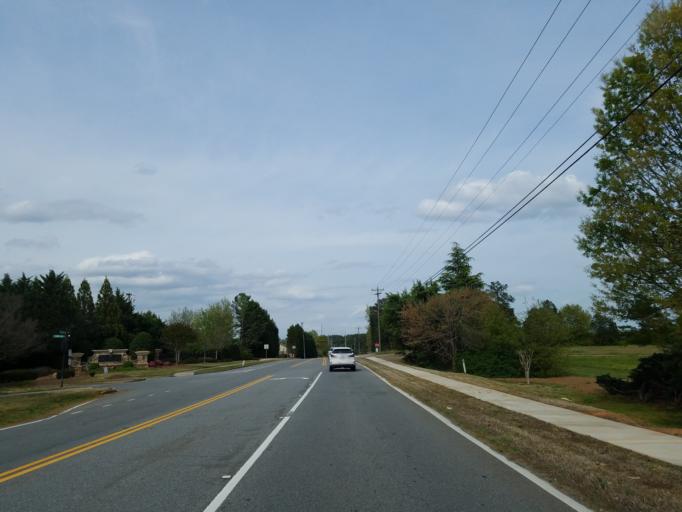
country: US
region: Georgia
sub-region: Fulton County
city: Johns Creek
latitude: 34.1144
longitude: -84.1797
